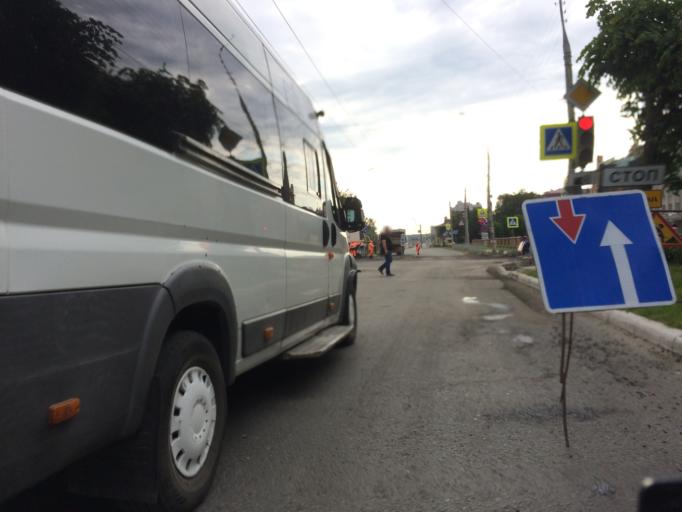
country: RU
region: Mariy-El
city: Yoshkar-Ola
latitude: 56.6405
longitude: 47.8955
